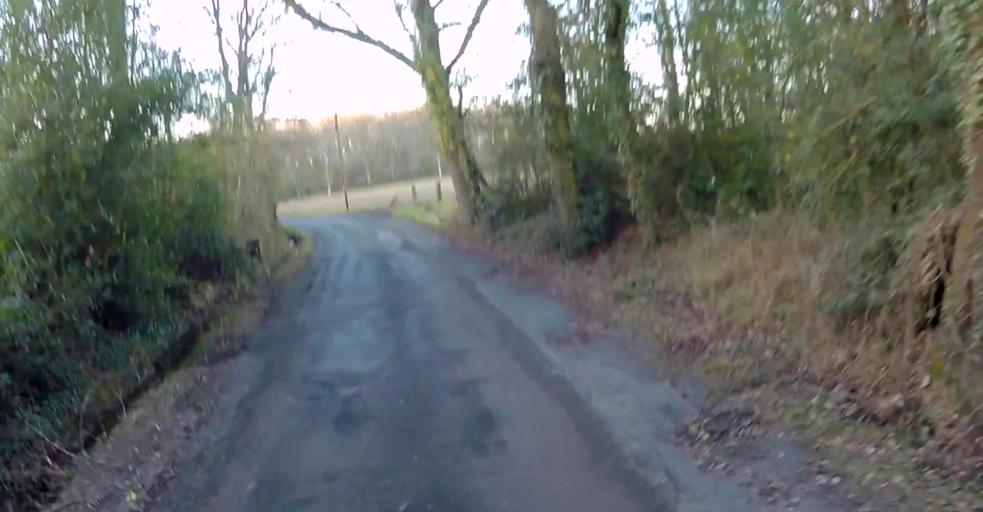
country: GB
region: England
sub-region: Hampshire
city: Hook
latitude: 51.3204
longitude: -0.9765
